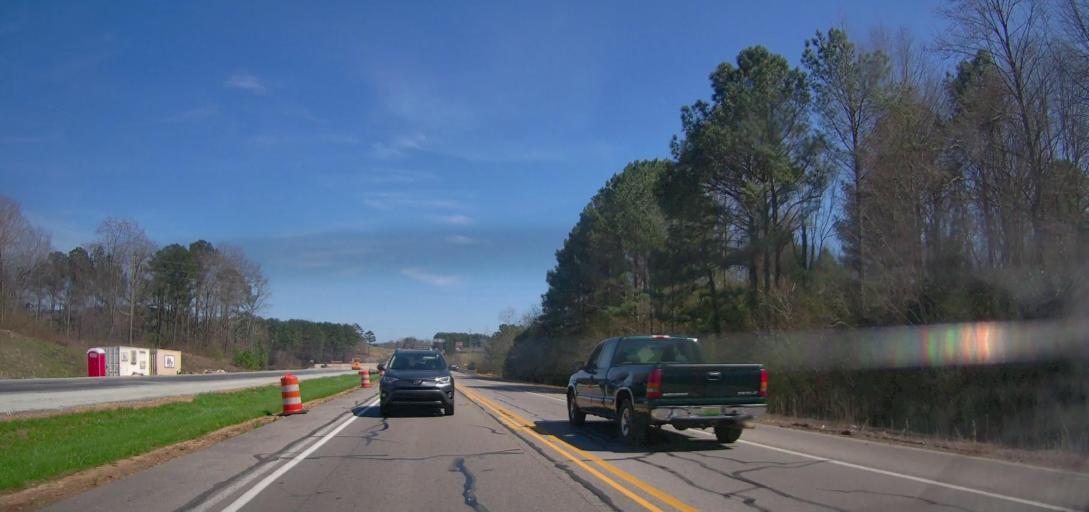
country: US
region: Alabama
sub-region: Cullman County
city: Cullman
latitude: 34.1993
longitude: -86.8147
